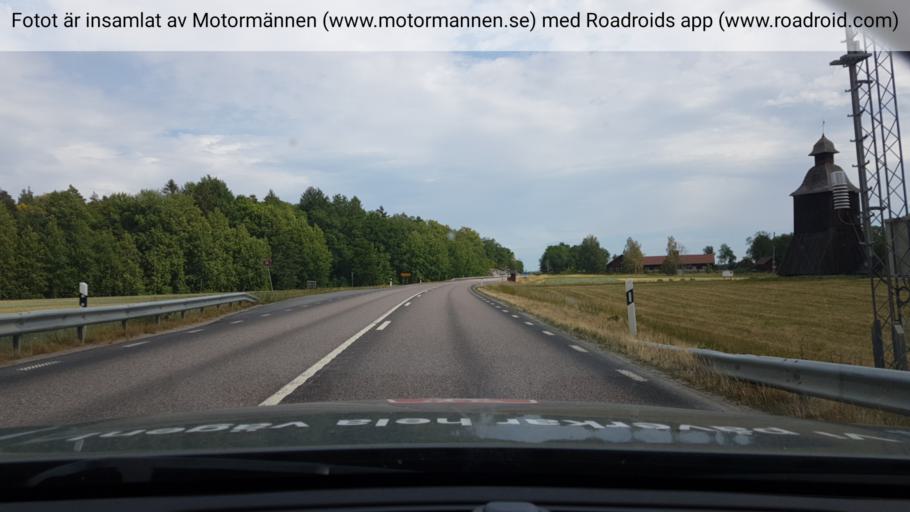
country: SE
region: Uppsala
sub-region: Enkopings Kommun
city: Orsundsbro
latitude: 59.8781
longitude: 17.2842
